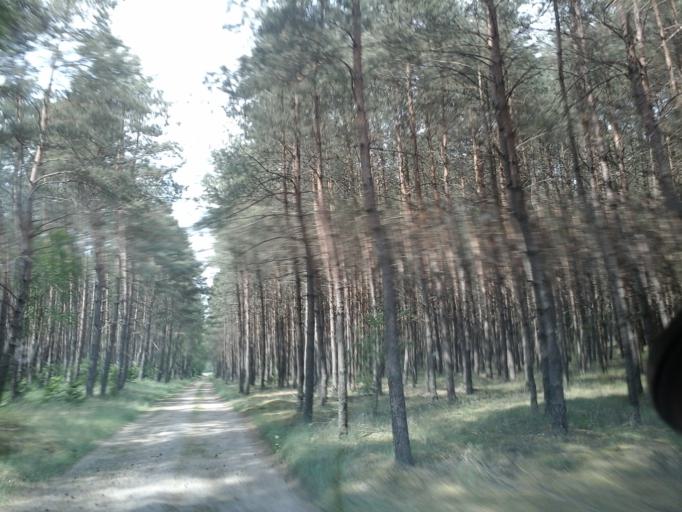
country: PL
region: West Pomeranian Voivodeship
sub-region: Powiat choszczenski
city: Drawno
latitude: 53.1228
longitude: 15.8538
